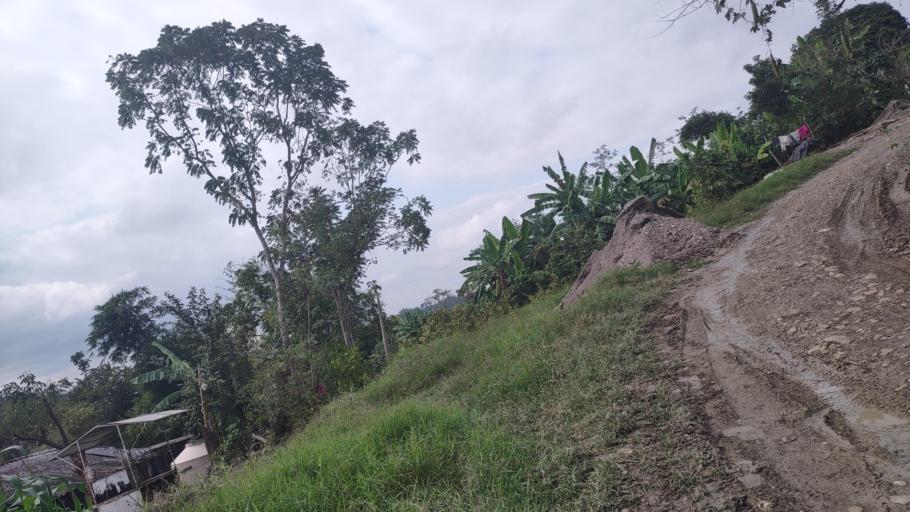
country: MX
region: Veracruz
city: Coatzintla
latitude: 20.4593
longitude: -97.4199
